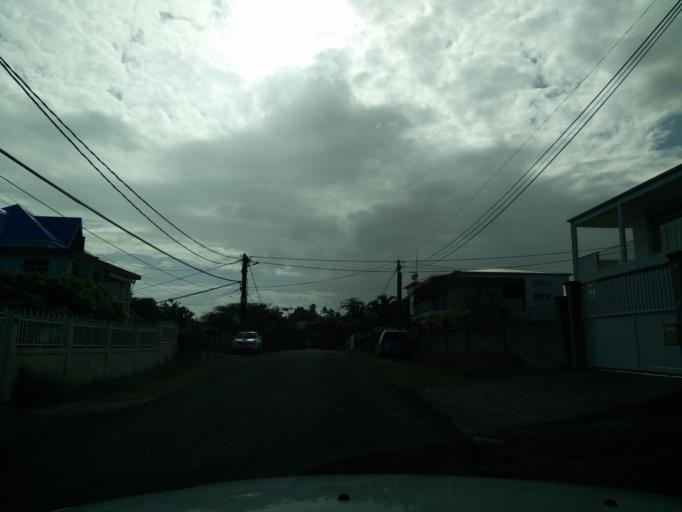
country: GP
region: Guadeloupe
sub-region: Guadeloupe
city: Sainte-Anne
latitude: 16.2308
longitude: -61.3784
